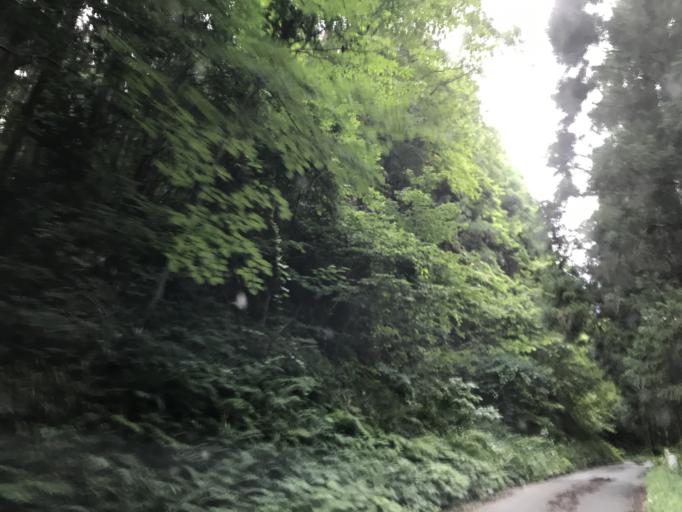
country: JP
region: Iwate
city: Ichinoseki
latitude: 38.8988
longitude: 141.0123
